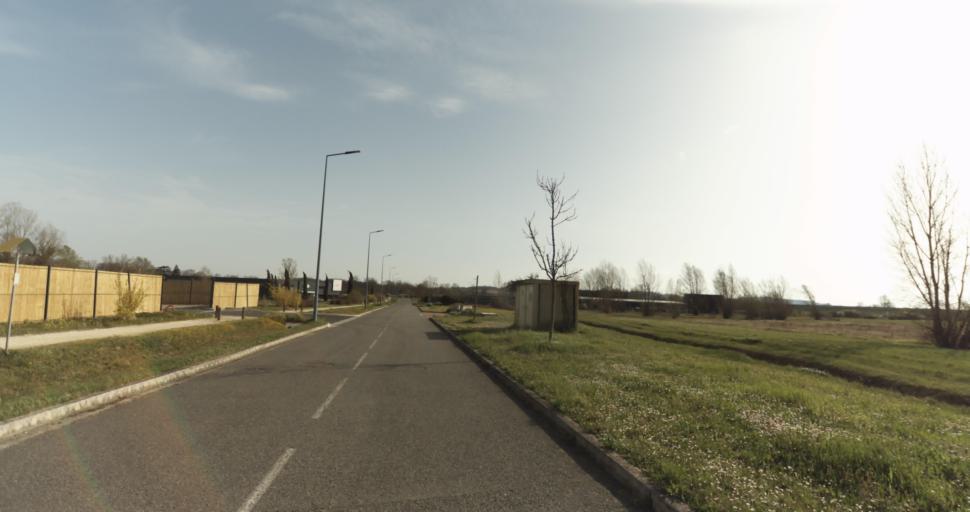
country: FR
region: Midi-Pyrenees
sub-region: Departement du Tarn
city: Saint-Sulpice-la-Pointe
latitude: 43.7659
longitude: 1.7143
